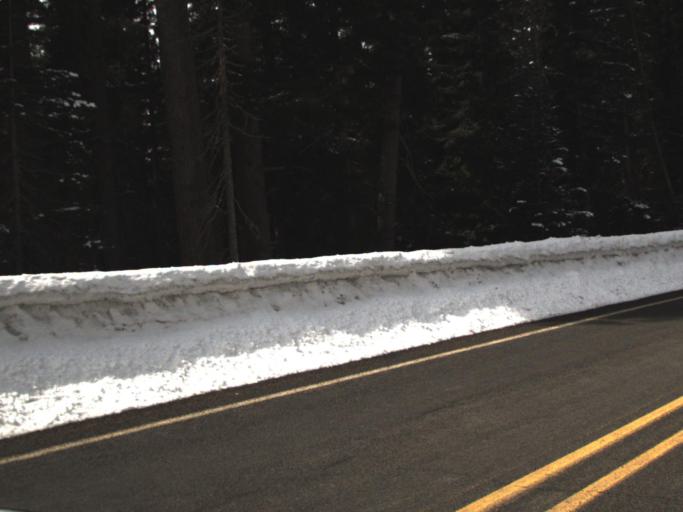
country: US
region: Washington
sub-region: Kittitas County
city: Cle Elum
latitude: 46.9135
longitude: -121.4034
